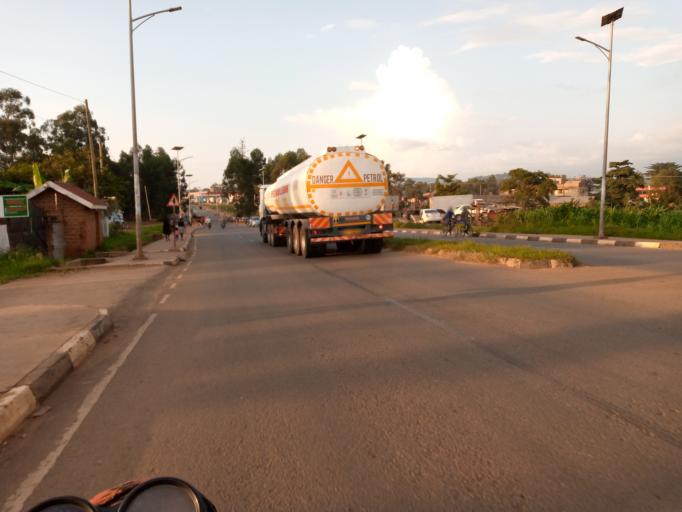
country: UG
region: Eastern Region
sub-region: Mbale District
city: Mbale
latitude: 1.0835
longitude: 34.1771
